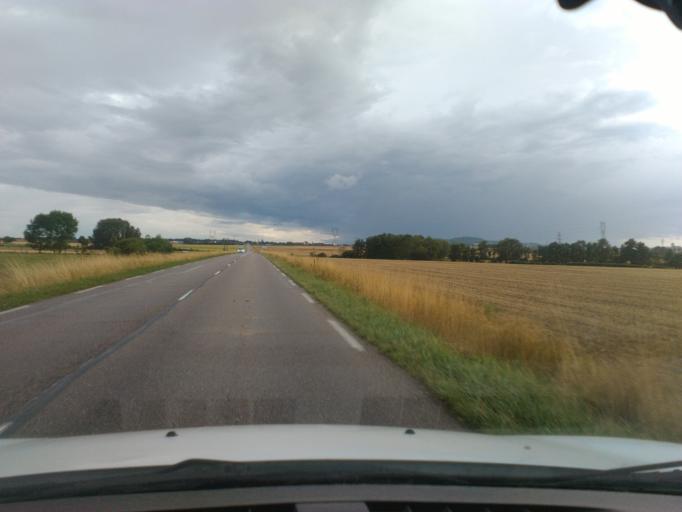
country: FR
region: Lorraine
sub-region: Departement de Meurthe-et-Moselle
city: Pulligny
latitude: 48.4931
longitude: 6.1462
